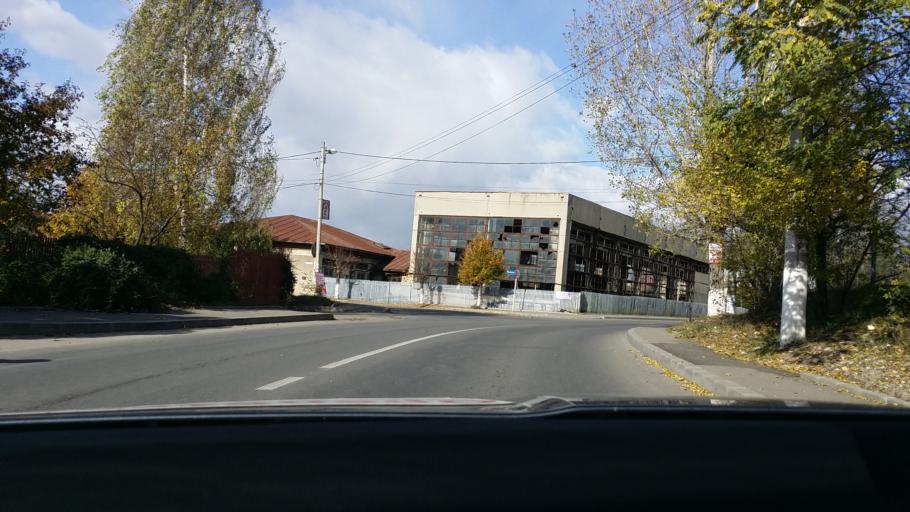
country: RO
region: Prahova
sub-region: Municipiul Campina
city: Campina
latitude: 45.1306
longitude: 25.7485
